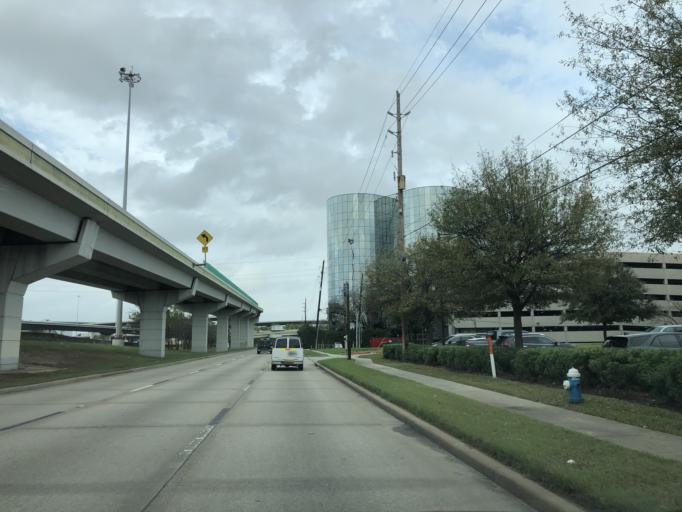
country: US
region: Texas
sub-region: Harris County
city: Aldine
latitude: 29.9359
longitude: -95.4117
